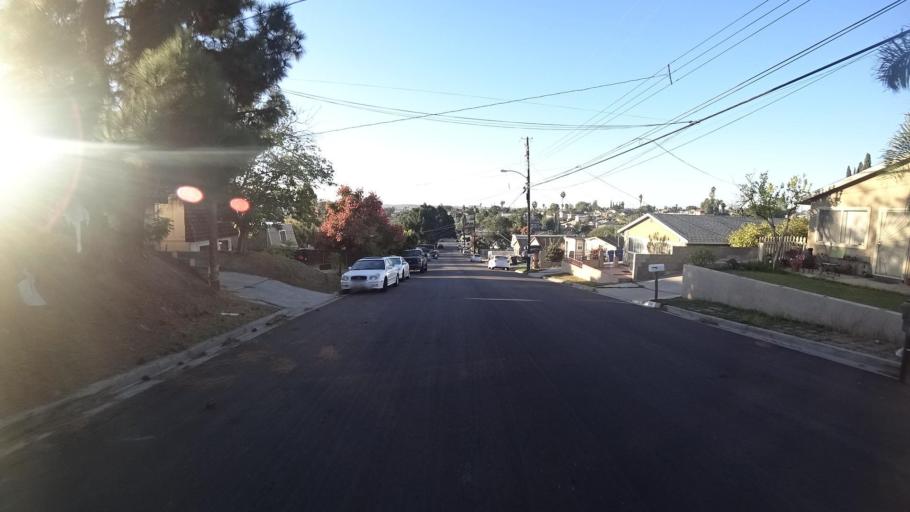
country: US
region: California
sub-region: San Diego County
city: La Presa
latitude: 32.7132
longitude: -116.9923
